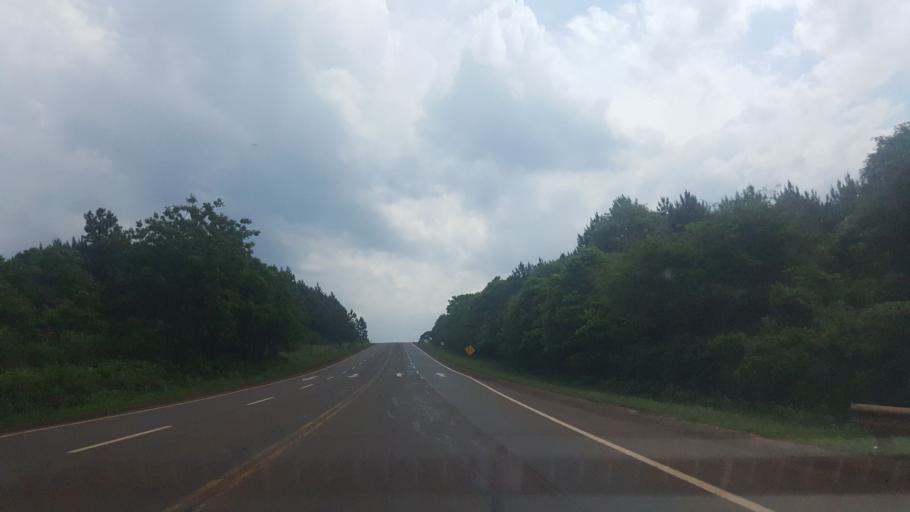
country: AR
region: Misiones
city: Santo Pipo
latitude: -27.1049
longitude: -55.3230
